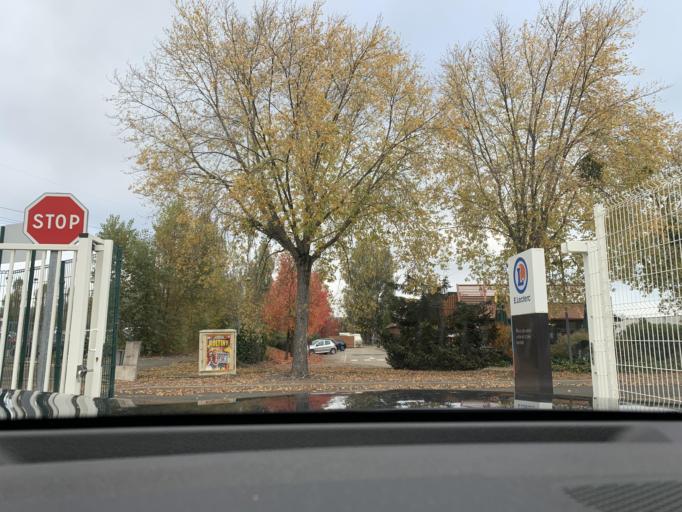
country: FR
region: Rhone-Alpes
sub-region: Departement du Rhone
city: Lozanne
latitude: 45.8557
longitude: 4.7032
